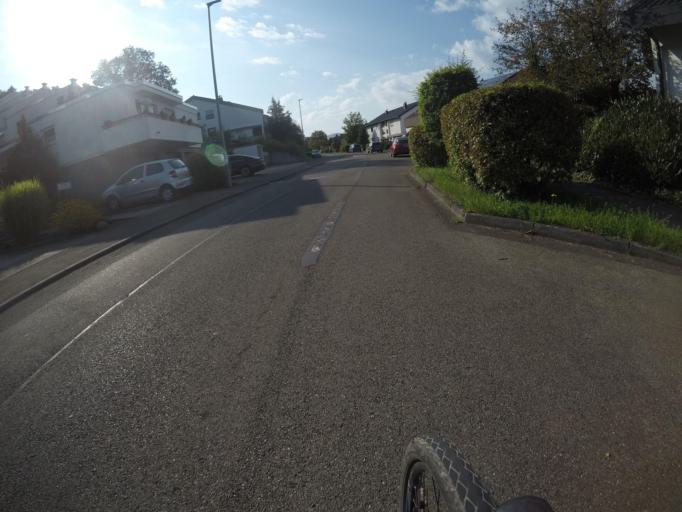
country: DE
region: Baden-Wuerttemberg
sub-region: Tuebingen Region
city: Riederich
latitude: 48.5591
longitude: 9.2720
